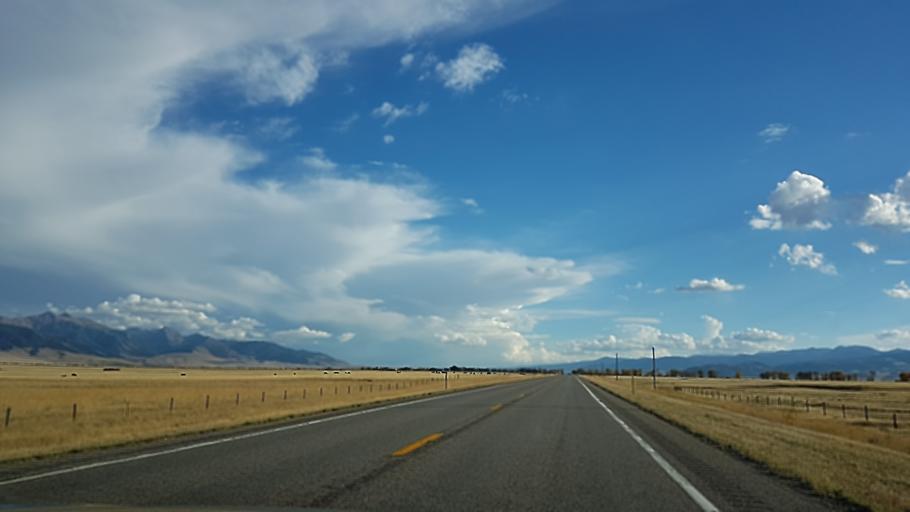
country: US
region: Montana
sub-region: Madison County
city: Virginia City
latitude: 45.2234
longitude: -111.6790
